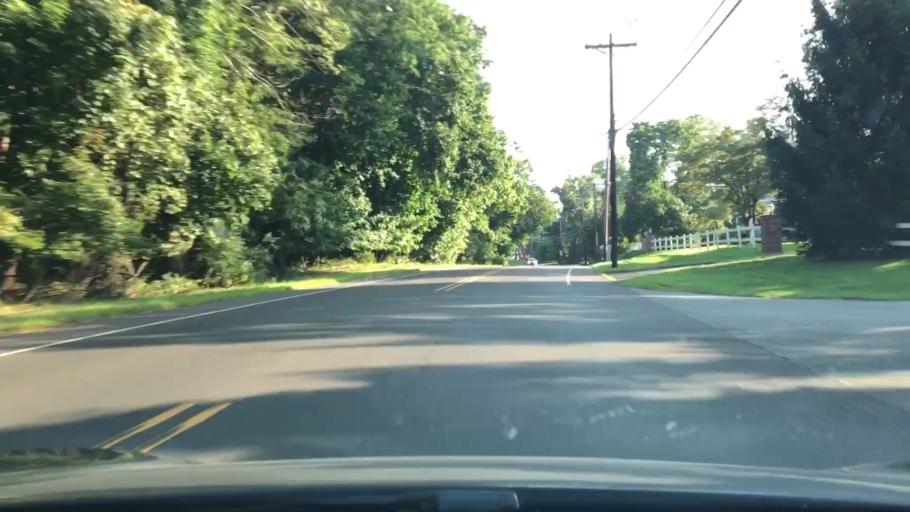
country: US
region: New Jersey
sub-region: Mercer County
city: Pennington
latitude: 40.3121
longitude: -74.7864
